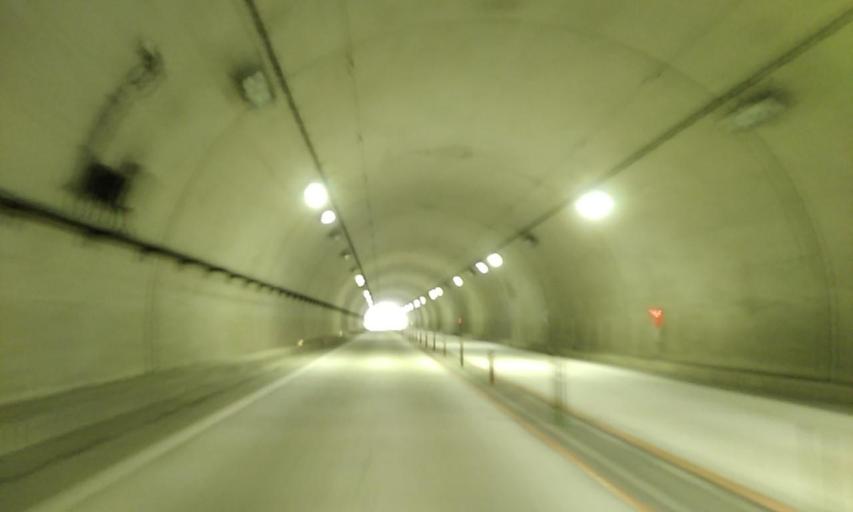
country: JP
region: Wakayama
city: Shingu
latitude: 33.6300
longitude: 135.9227
